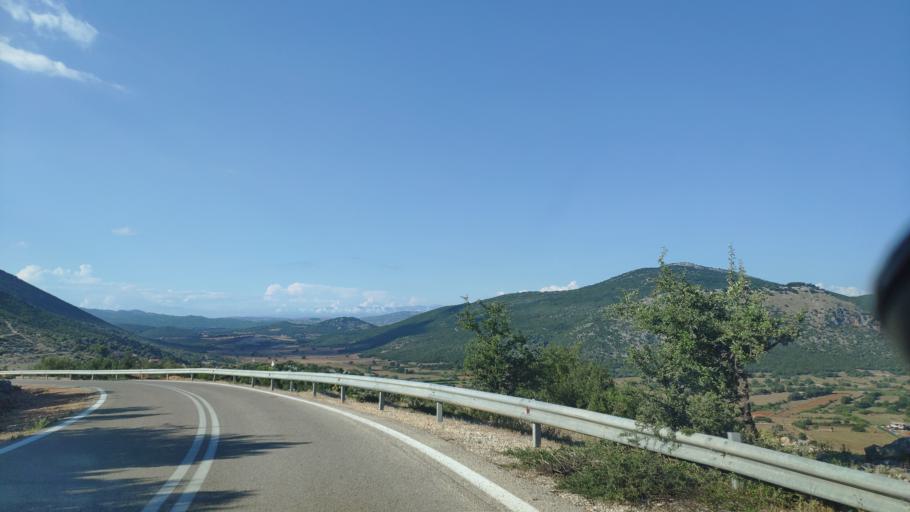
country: GR
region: West Greece
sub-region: Nomos Aitolias kai Akarnanias
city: Archontochorion
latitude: 38.6976
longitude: 21.0806
